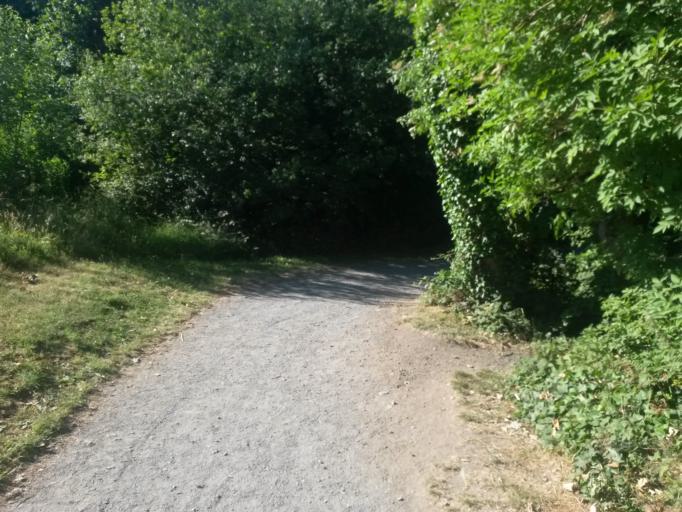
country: IE
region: Leinster
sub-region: Wicklow
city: Blessington
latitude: 53.1586
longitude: -6.5345
